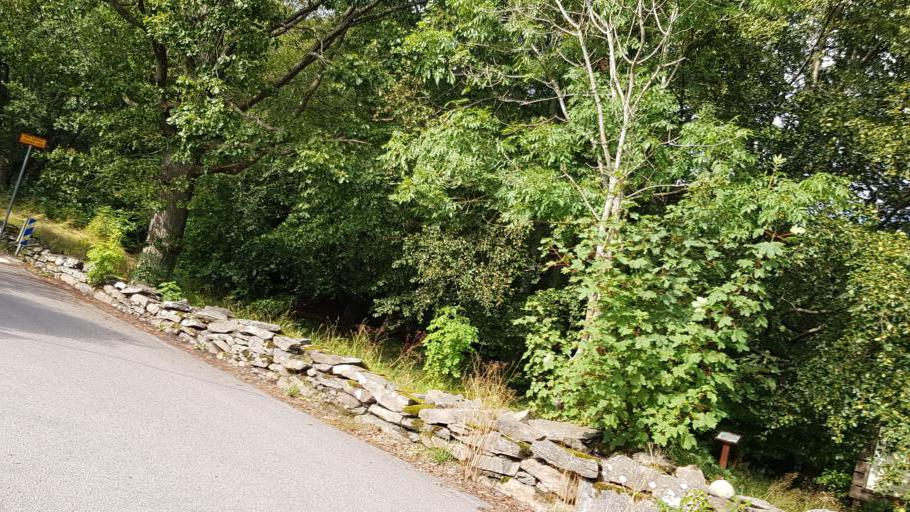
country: SE
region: Vaestra Goetaland
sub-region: Harryda Kommun
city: Molnlycke
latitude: 57.6621
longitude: 12.1220
